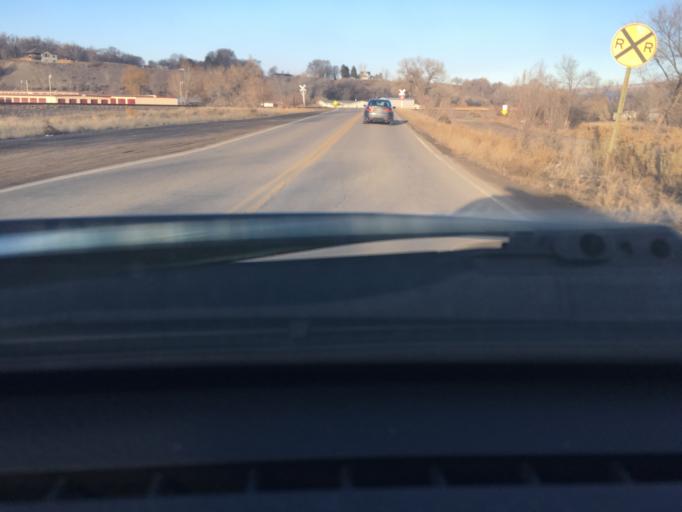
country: US
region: Colorado
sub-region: Delta County
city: Delta
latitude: 38.7405
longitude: -108.0812
